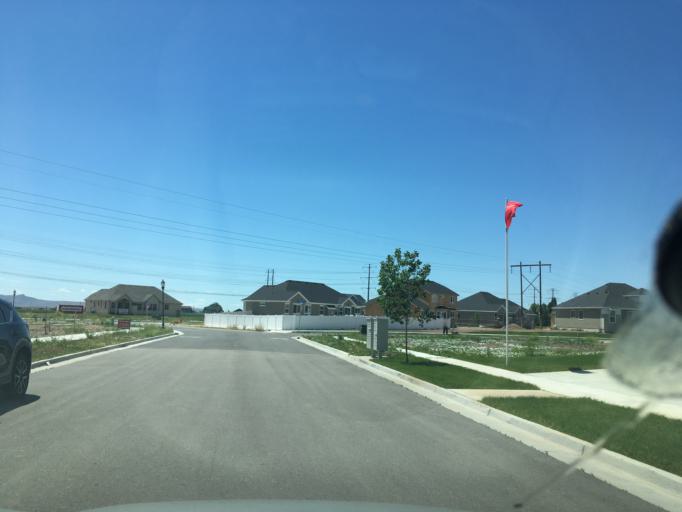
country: US
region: Utah
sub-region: Davis County
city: Layton
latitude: 41.0509
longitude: -111.9978
